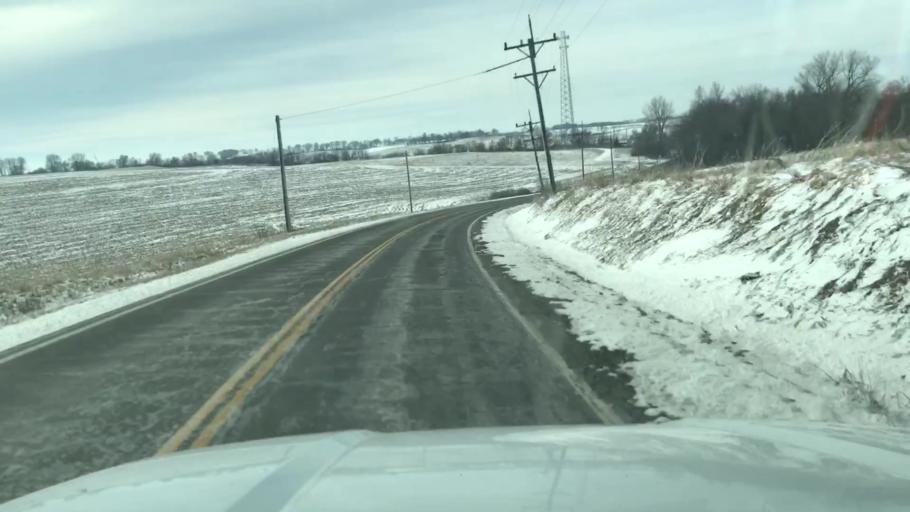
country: US
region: Missouri
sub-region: Holt County
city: Oregon
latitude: 40.0496
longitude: -95.1360
